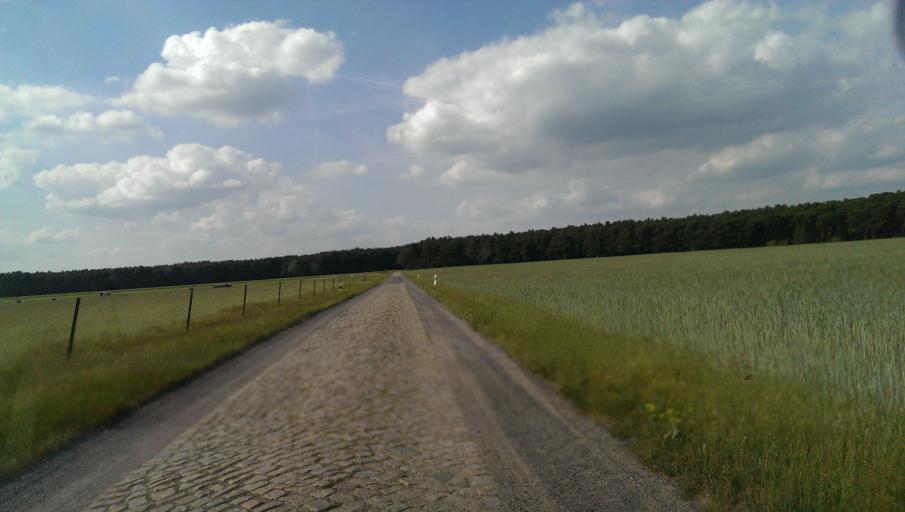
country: DE
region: Brandenburg
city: Linthe
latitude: 52.1548
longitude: 12.7166
